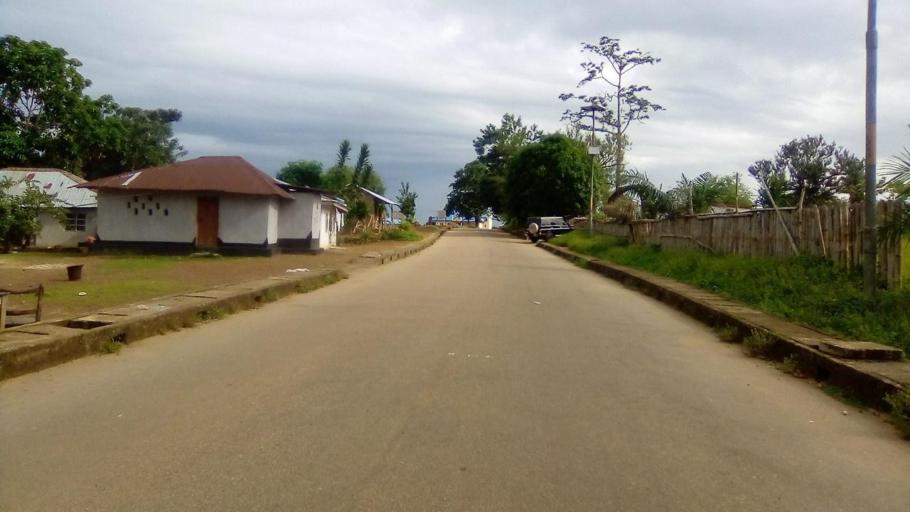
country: SL
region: Southern Province
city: Pujehun
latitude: 7.3668
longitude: -11.7258
